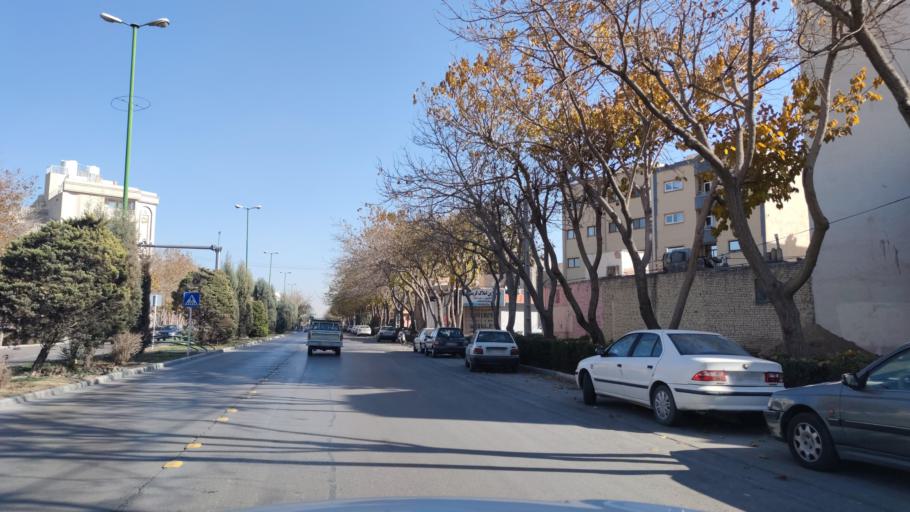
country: IR
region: Isfahan
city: Isfahan
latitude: 32.6800
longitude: 51.6556
